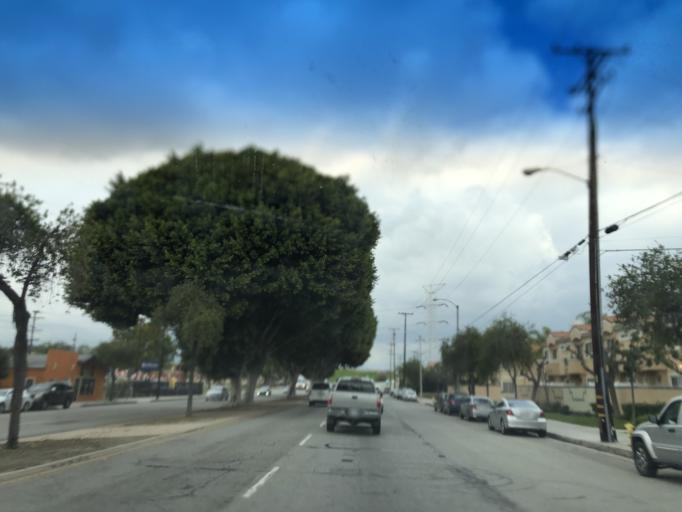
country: US
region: California
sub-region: Los Angeles County
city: Montebello
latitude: 34.0149
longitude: -118.0795
